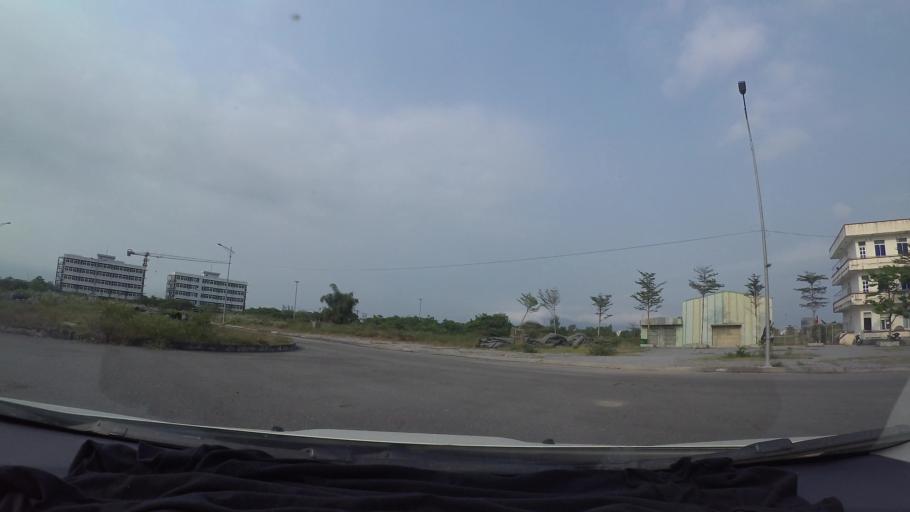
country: VN
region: Da Nang
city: Lien Chieu
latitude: 16.0472
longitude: 108.1602
